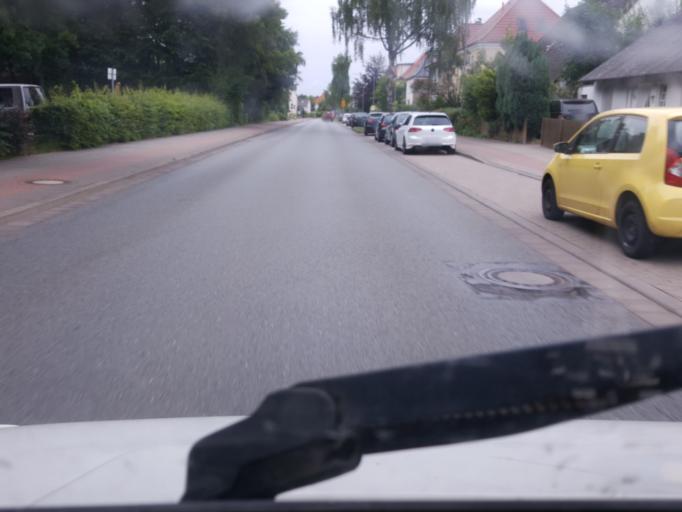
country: DE
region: North Rhine-Westphalia
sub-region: Regierungsbezirk Detmold
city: Minden
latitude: 52.2966
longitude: 8.8932
